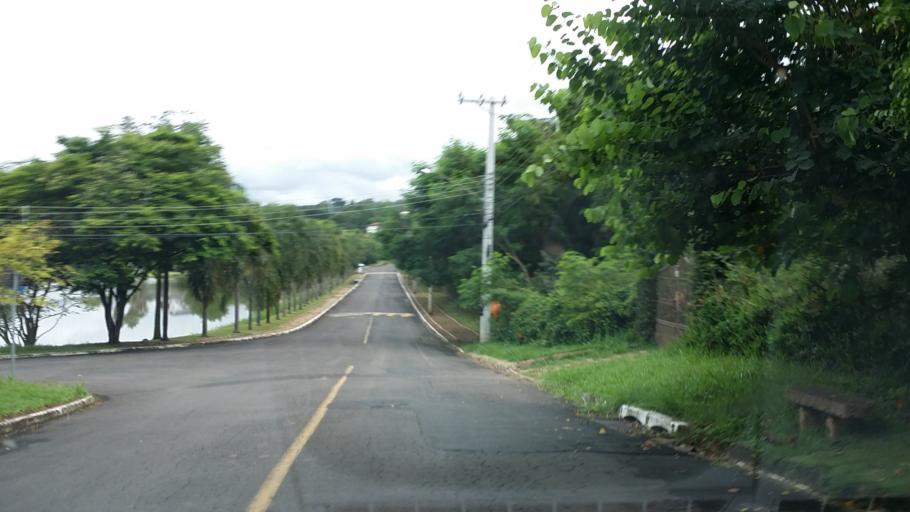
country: BR
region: Sao Paulo
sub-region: Indaiatuba
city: Indaiatuba
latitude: -23.1378
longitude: -47.1915
